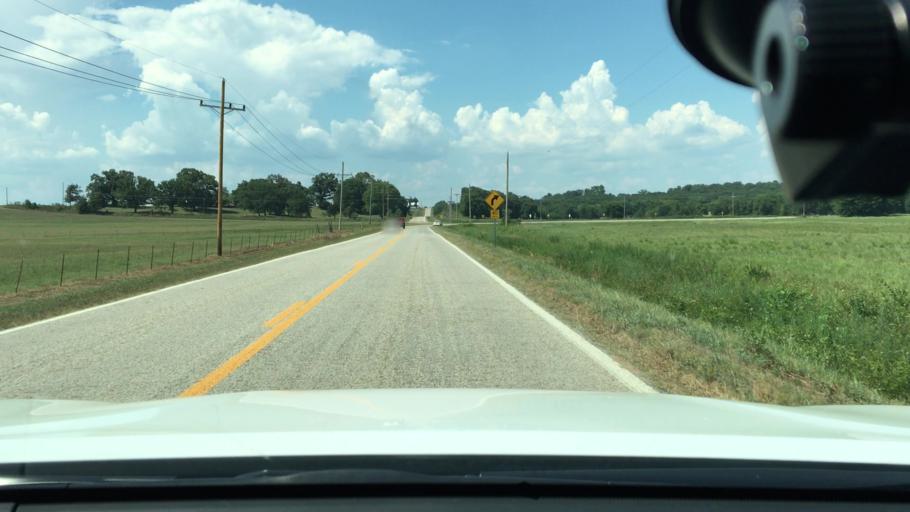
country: US
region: Arkansas
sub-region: Logan County
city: Paris
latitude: 35.3344
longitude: -93.6319
